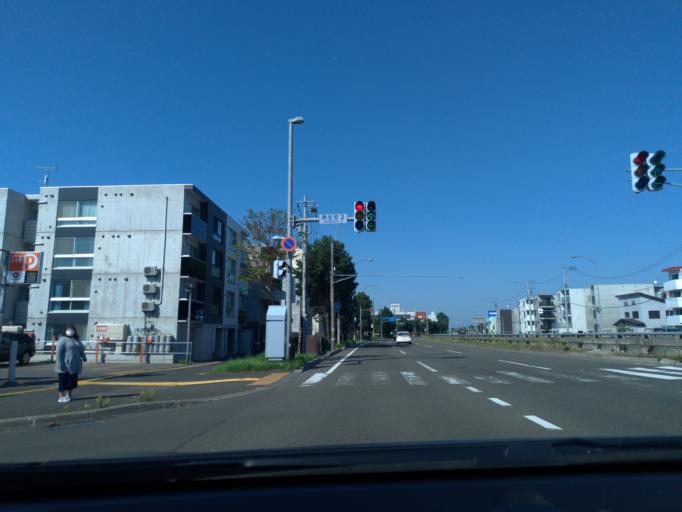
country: JP
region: Hokkaido
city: Sapporo
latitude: 43.1098
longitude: 141.3434
